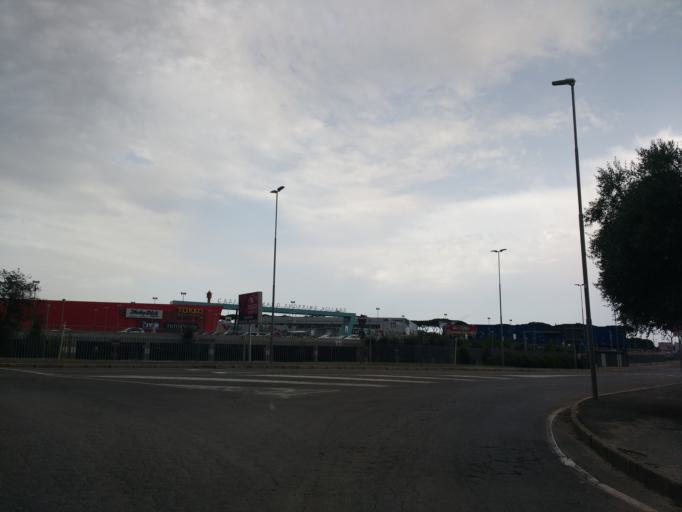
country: IT
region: Latium
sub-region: Citta metropolitana di Roma Capitale
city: Monte Migliore-La Selvotta
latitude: 41.7143
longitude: 12.4436
